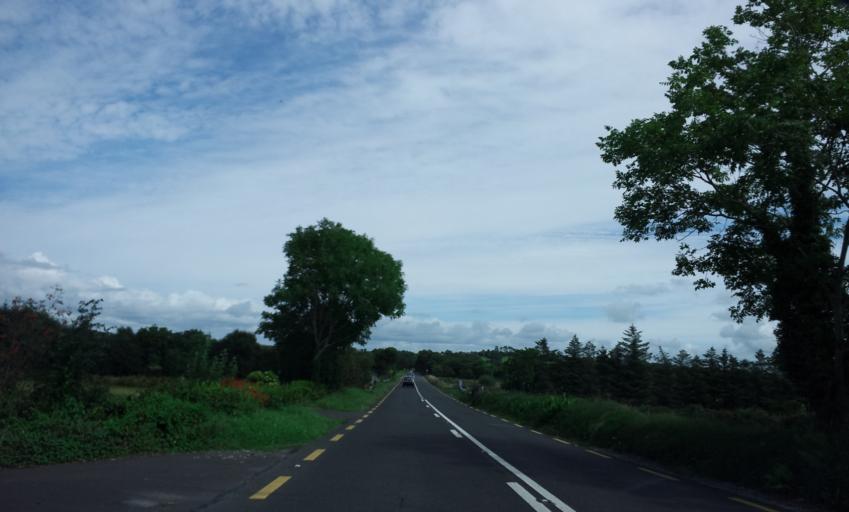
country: IE
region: Munster
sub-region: Ciarrai
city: Killorglin
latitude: 52.0958
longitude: -9.8351
